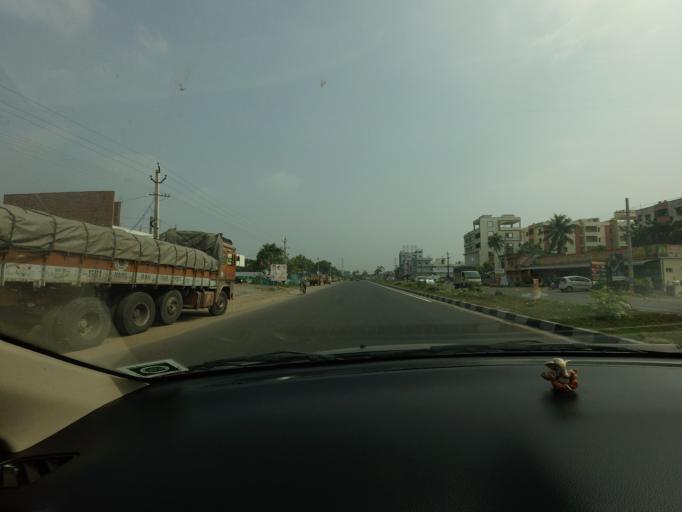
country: IN
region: Andhra Pradesh
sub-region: Krishna
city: Yanamalakuduru
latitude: 16.4711
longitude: 80.7210
